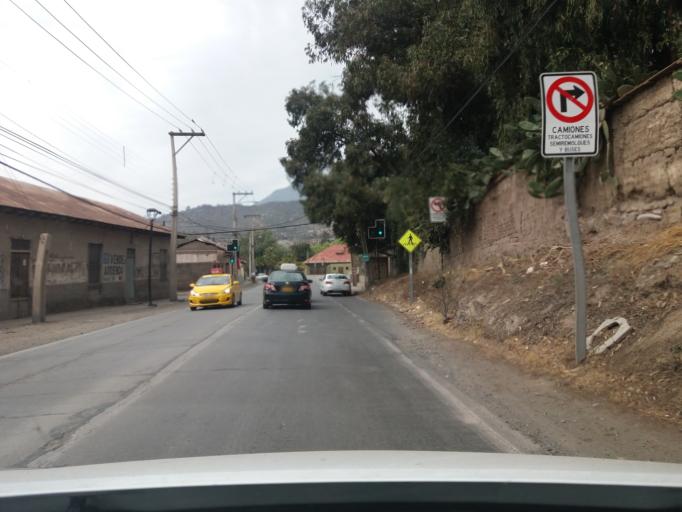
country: CL
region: Valparaiso
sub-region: Provincia de Los Andes
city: Los Andes
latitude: -32.8367
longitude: -70.5826
